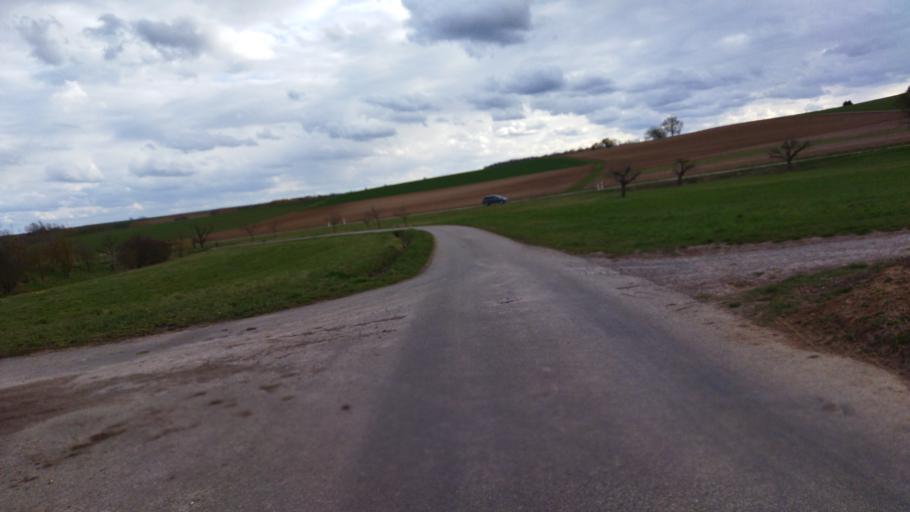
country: DE
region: Baden-Wuerttemberg
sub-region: Regierungsbezirk Stuttgart
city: Nordheim
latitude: 49.1185
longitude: 9.1119
